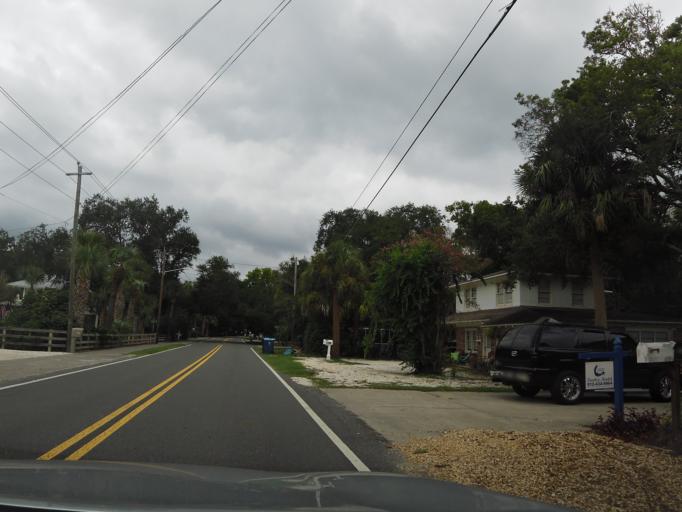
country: US
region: Georgia
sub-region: Glynn County
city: Saint Simons Island
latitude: 31.1384
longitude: -81.3832
